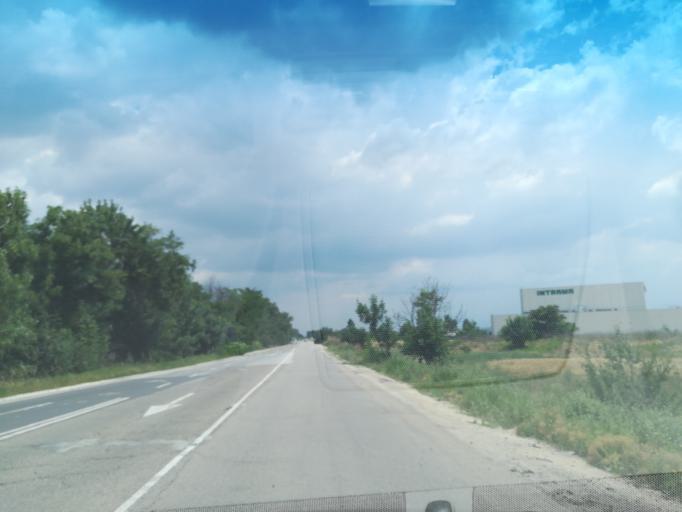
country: BG
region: Plovdiv
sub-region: Obshtina Plovdiv
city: Plovdiv
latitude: 42.2005
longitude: 24.6713
